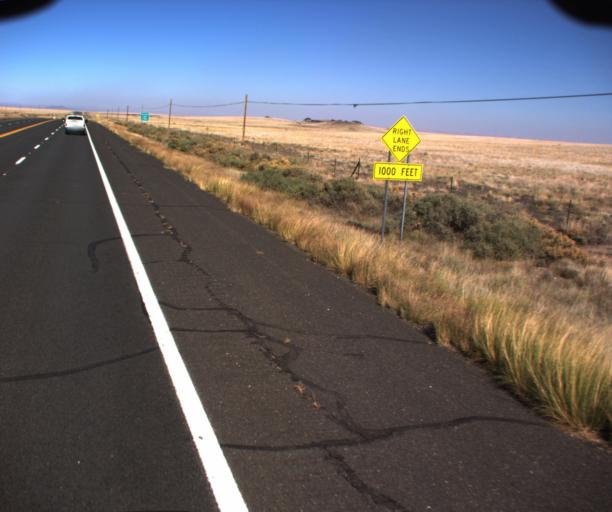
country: US
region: Arizona
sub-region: Coconino County
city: Flagstaff
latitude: 35.6308
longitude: -111.5199
